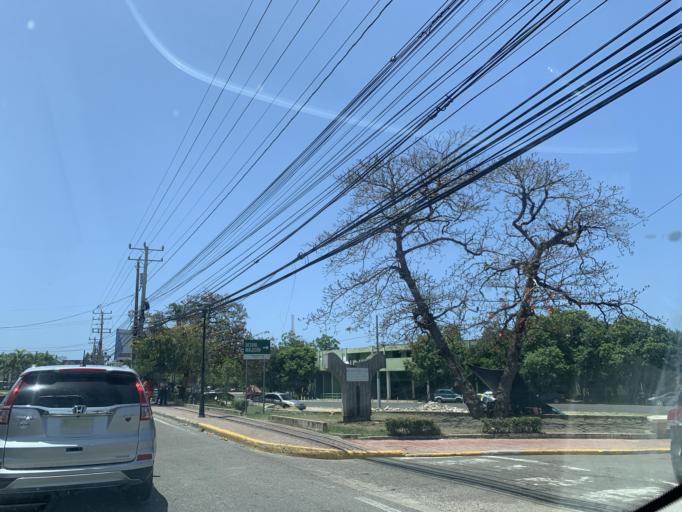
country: DO
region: Puerto Plata
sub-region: Puerto Plata
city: Puerto Plata
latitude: 19.7816
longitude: -70.6720
